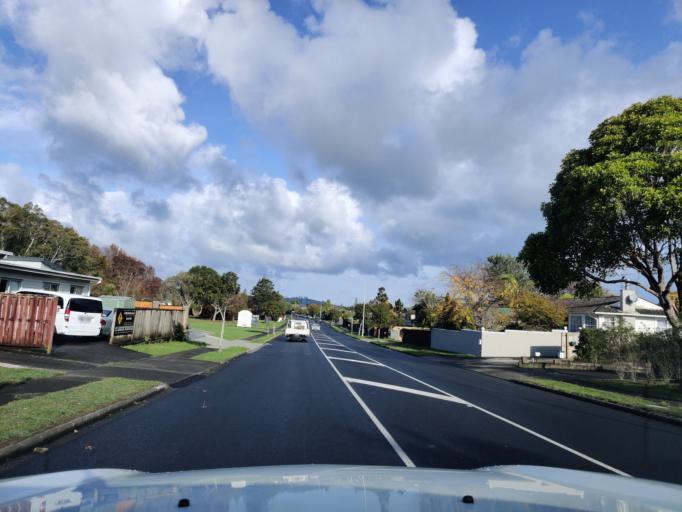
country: NZ
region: Auckland
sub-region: Auckland
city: Pakuranga
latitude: -36.9083
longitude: 174.8977
